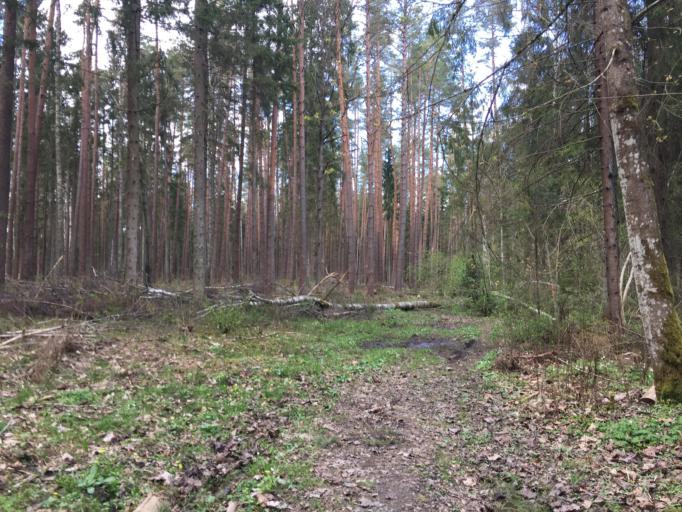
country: LV
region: Baldone
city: Baldone
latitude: 56.7495
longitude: 24.3817
